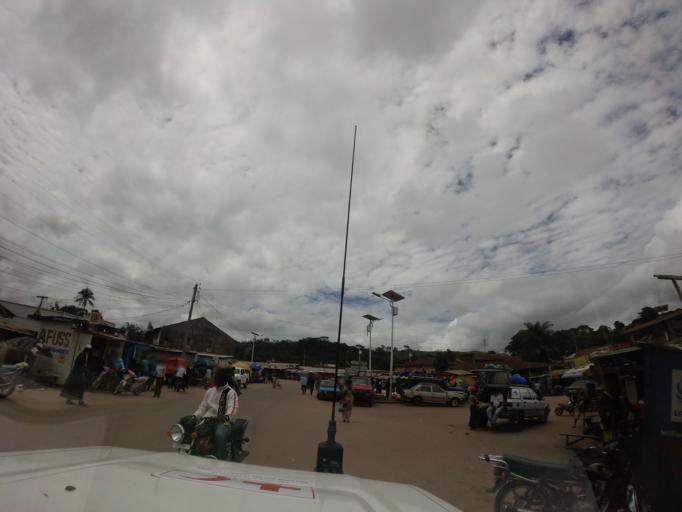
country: GN
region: Nzerekore
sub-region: Macenta
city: Macenta
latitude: 8.5464
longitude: -9.4690
